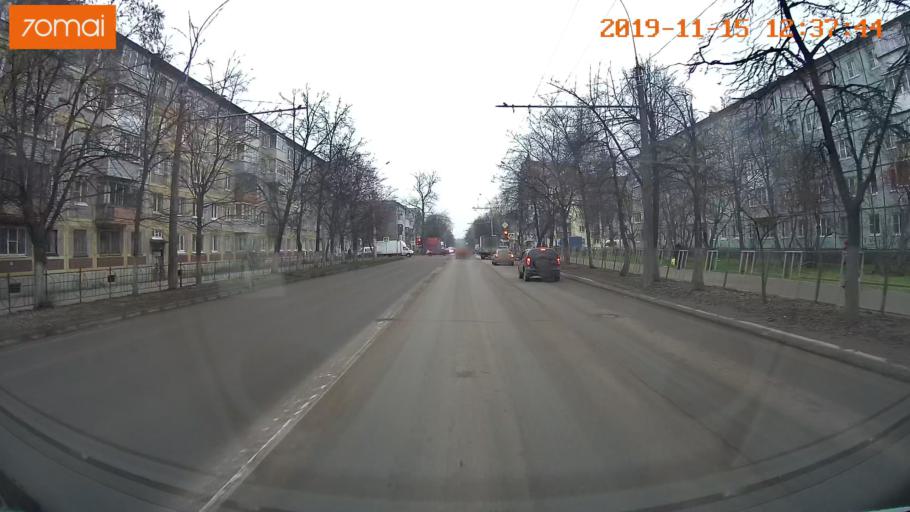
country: RU
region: Vologda
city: Vologda
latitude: 59.2071
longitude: 39.9022
